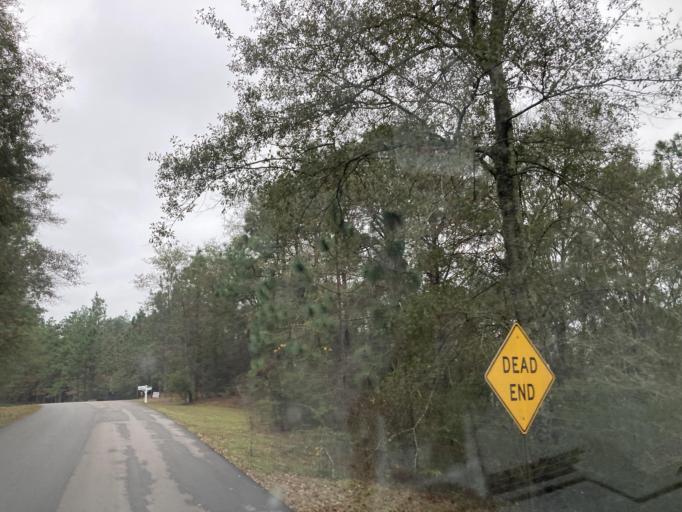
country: US
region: Mississippi
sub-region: Lamar County
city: Purvis
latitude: 31.1584
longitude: -89.4235
